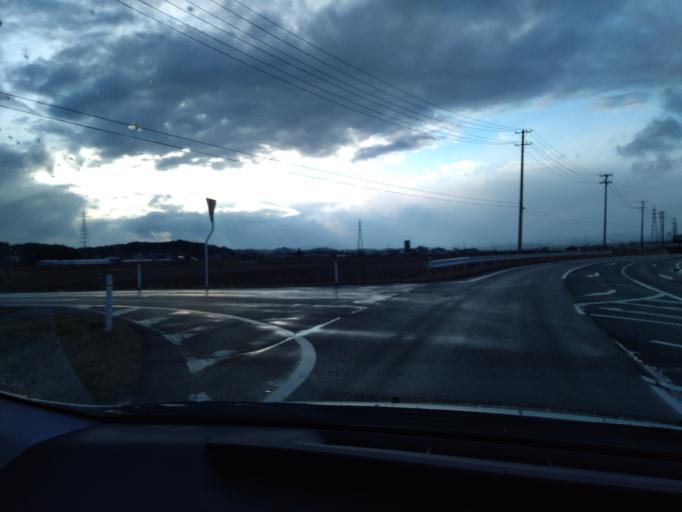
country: JP
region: Iwate
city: Ichinoseki
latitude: 38.7970
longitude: 141.0781
